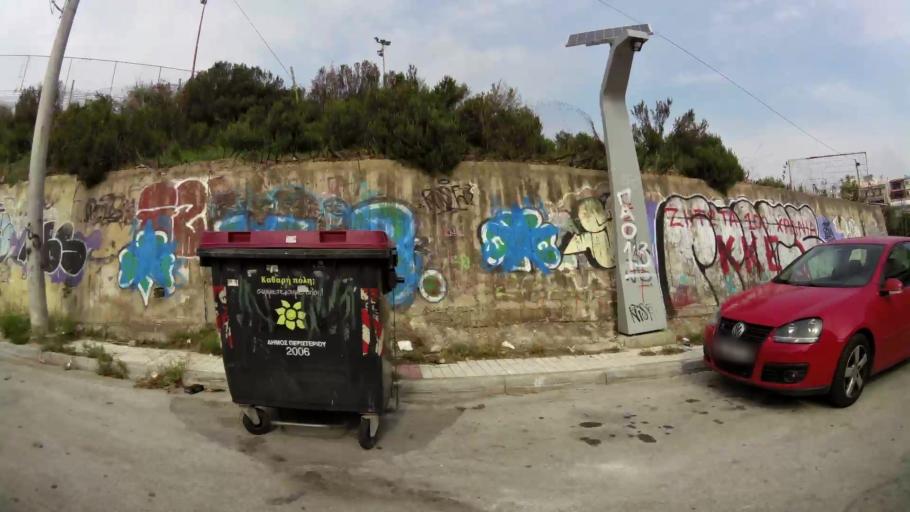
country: GR
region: Attica
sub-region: Nomarchia Athinas
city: Petroupolis
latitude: 38.0289
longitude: 23.6737
